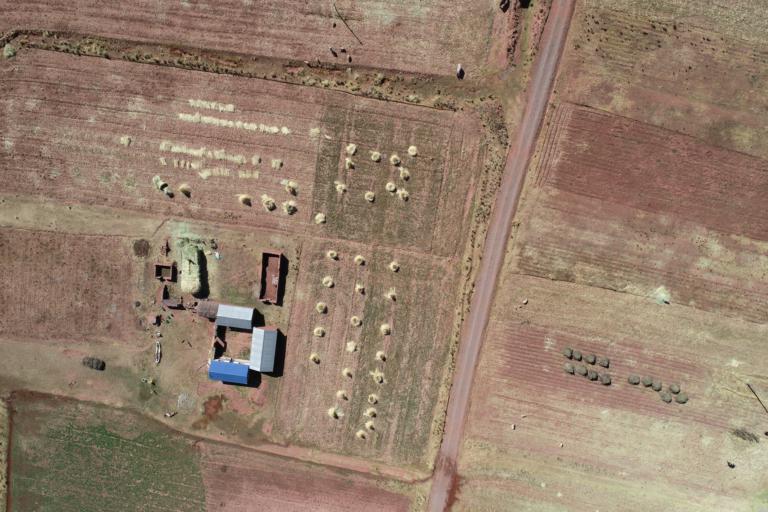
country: BO
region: La Paz
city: Tiahuanaco
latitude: -16.5936
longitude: -68.7575
